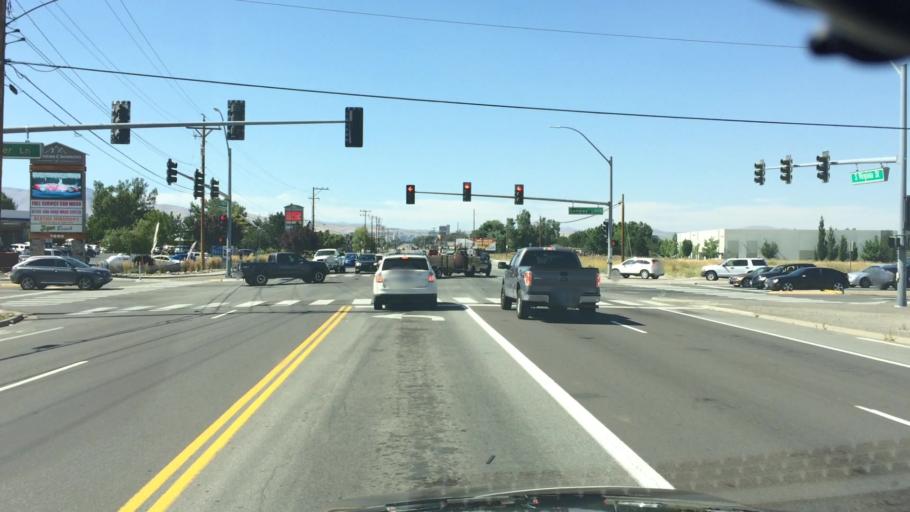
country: US
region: Nevada
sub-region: Washoe County
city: Reno
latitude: 39.4559
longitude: -119.7790
